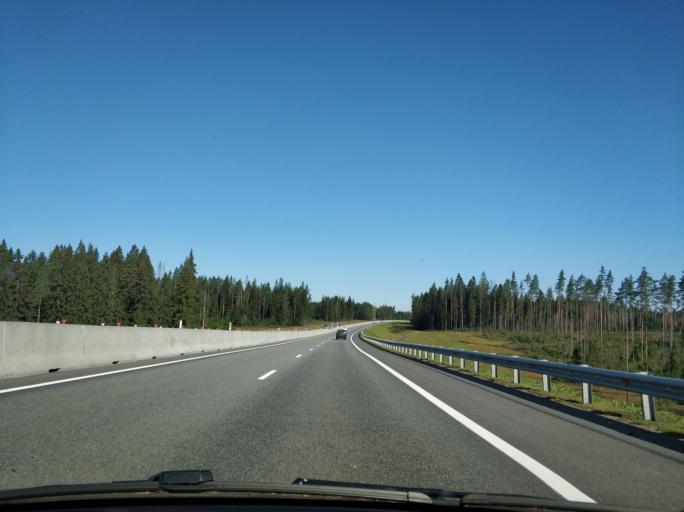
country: RU
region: Leningrad
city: Sosnovo
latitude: 60.5183
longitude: 30.1771
